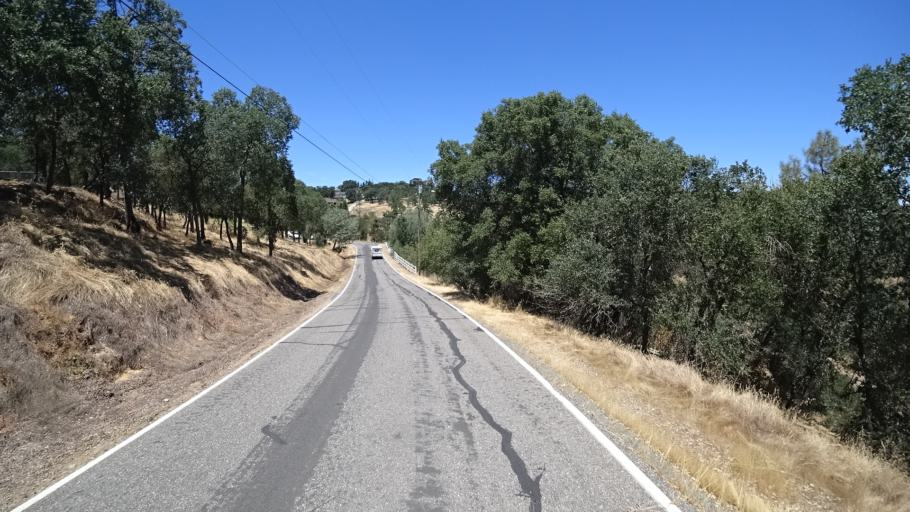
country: US
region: California
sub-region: Calaveras County
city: Rancho Calaveras
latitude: 38.1489
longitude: -120.8394
